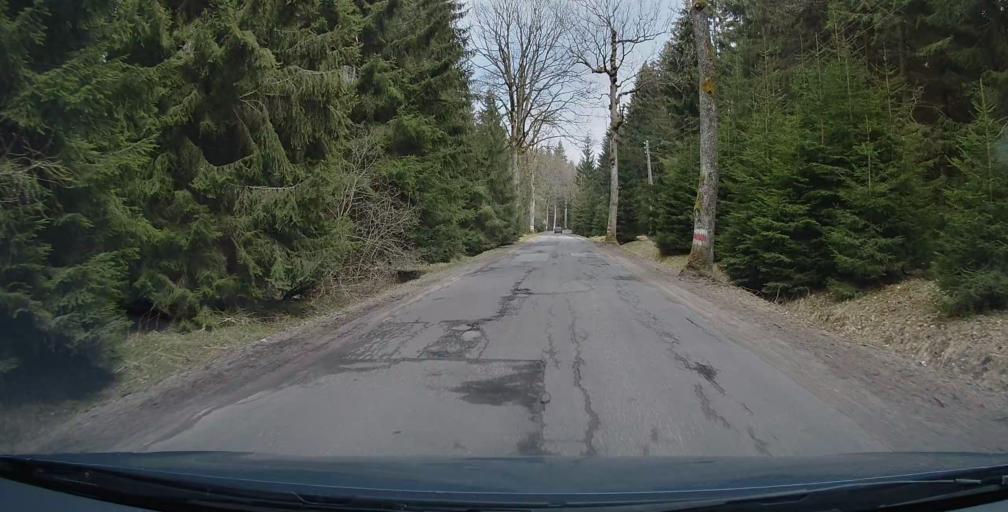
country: PL
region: Lower Silesian Voivodeship
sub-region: Powiat klodzki
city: Radkow
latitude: 50.4766
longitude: 16.3609
